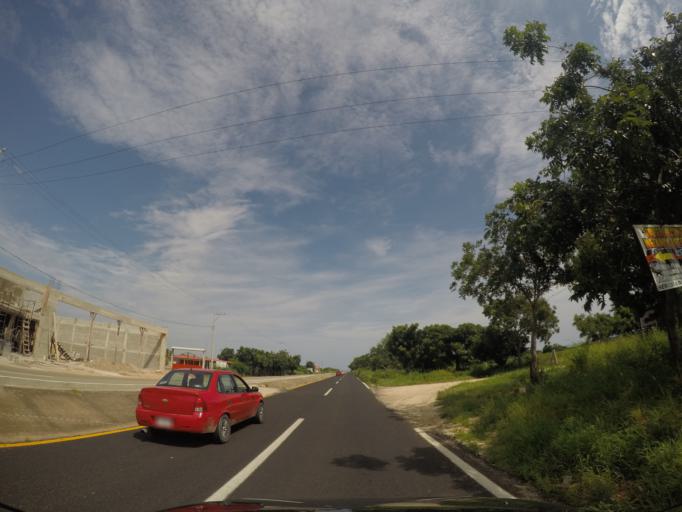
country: MX
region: Oaxaca
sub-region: Santa Maria Colotepec
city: Brisas de Zicatela
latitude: 15.8219
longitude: -97.0161
